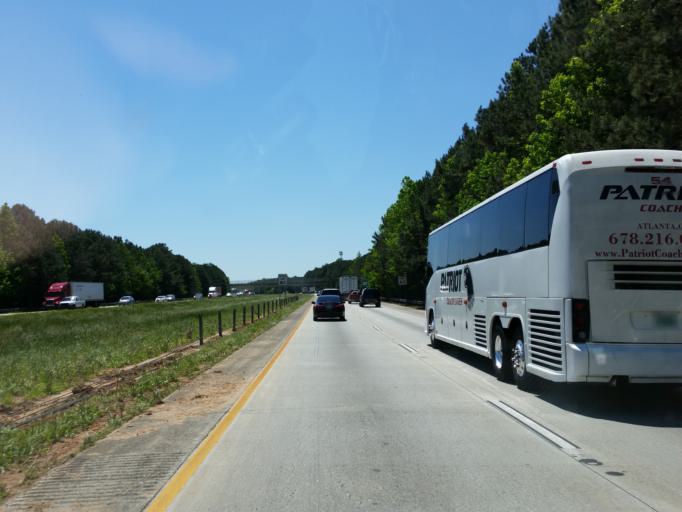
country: US
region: Georgia
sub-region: Clayton County
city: Lake City
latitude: 33.5873
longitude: -84.2815
